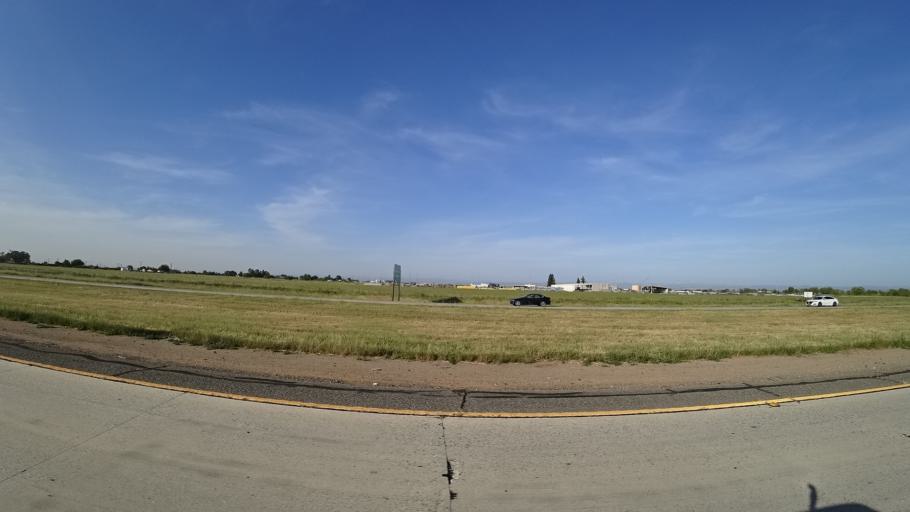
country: US
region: California
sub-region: Yuba County
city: Olivehurst
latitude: 39.0625
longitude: -121.5108
